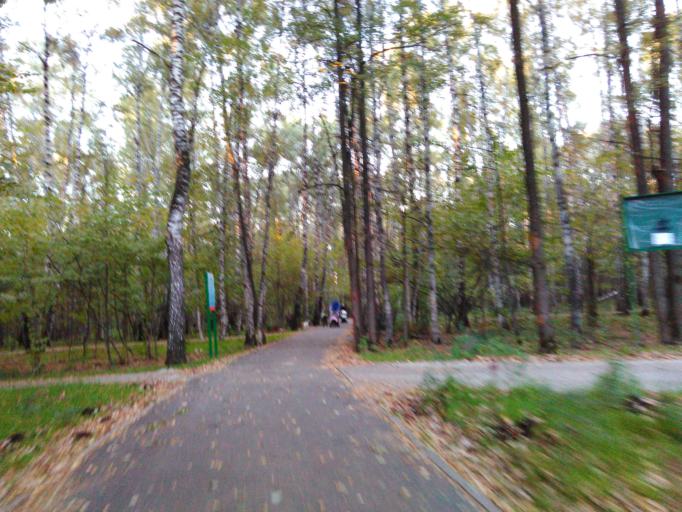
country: RU
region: Moscow
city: Troparevo
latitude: 55.6535
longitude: 37.5043
